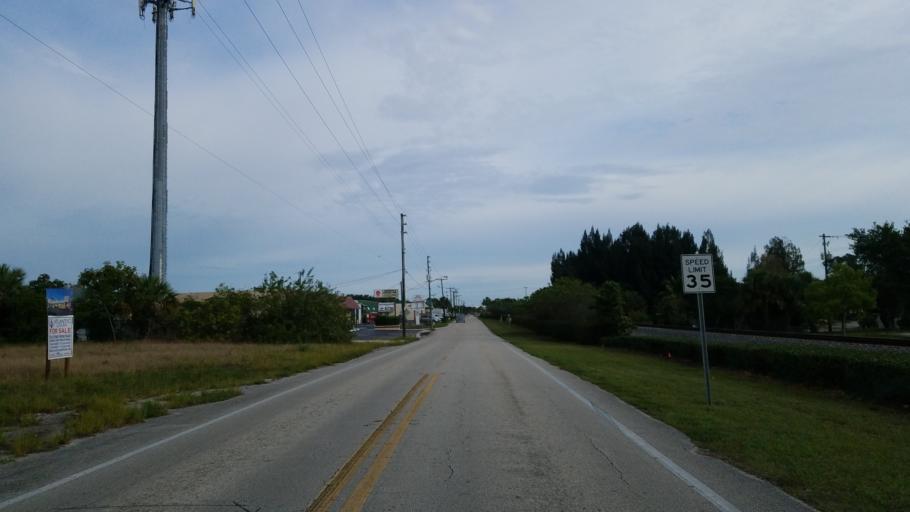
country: US
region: Florida
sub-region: Martin County
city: Stuart
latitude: 27.1908
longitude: -80.2464
